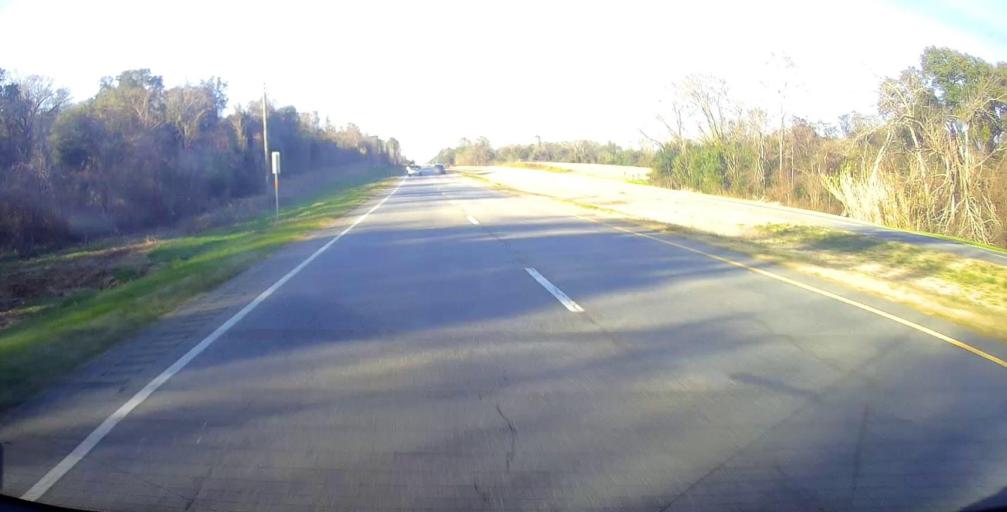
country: US
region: Georgia
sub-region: Lee County
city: Leesburg
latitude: 31.6951
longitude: -84.1728
